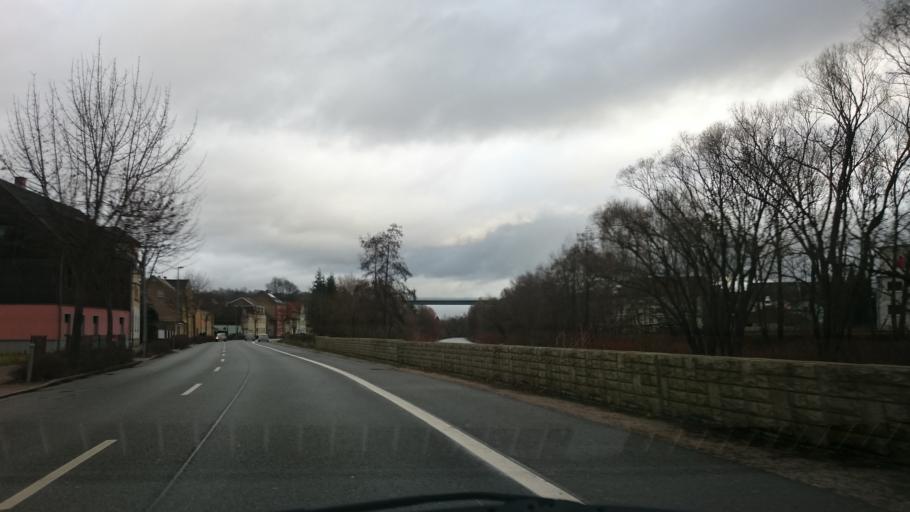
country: DE
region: Saxony
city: Wilkau-Hasslau
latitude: 50.6759
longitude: 12.5172
